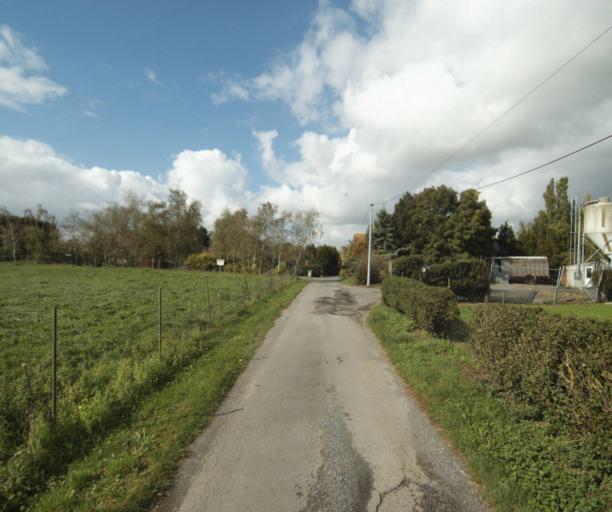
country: FR
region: Nord-Pas-de-Calais
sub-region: Departement du Nord
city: Frelinghien
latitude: 50.7229
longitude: 2.9381
